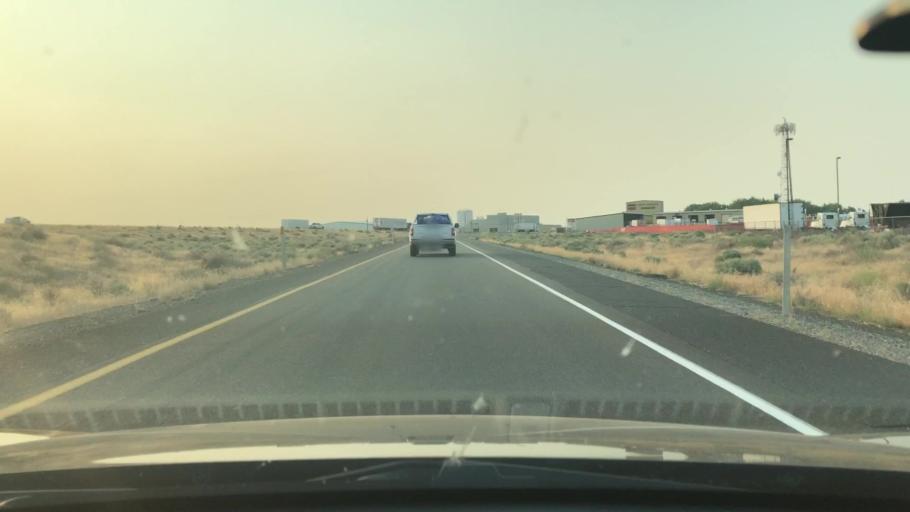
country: US
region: Washington
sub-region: Franklin County
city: Pasco
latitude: 46.2531
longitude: -119.0812
